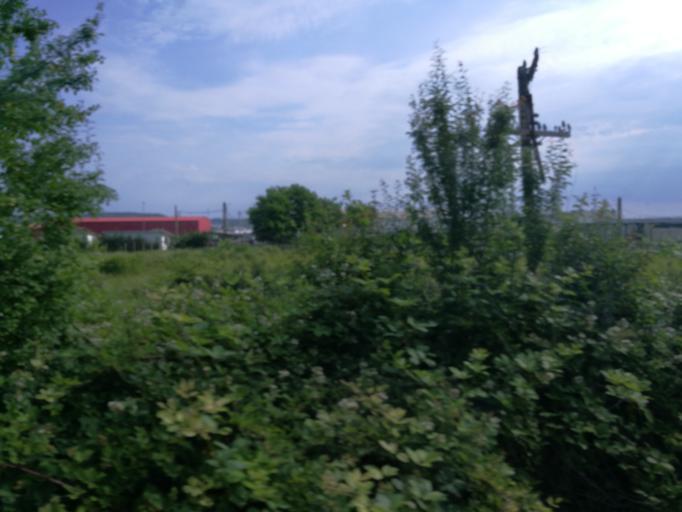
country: RO
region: Arges
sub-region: Comuna Bradu
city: Geamana
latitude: 44.8299
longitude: 24.9187
